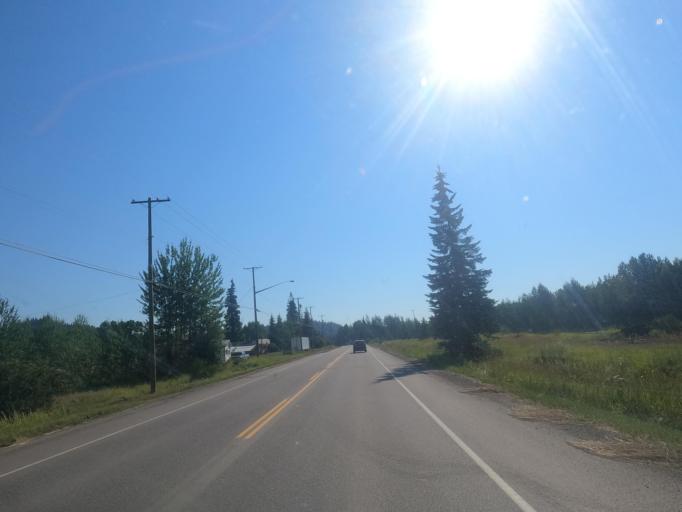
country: CA
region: British Columbia
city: Burns Lake
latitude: 54.0851
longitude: -125.0179
